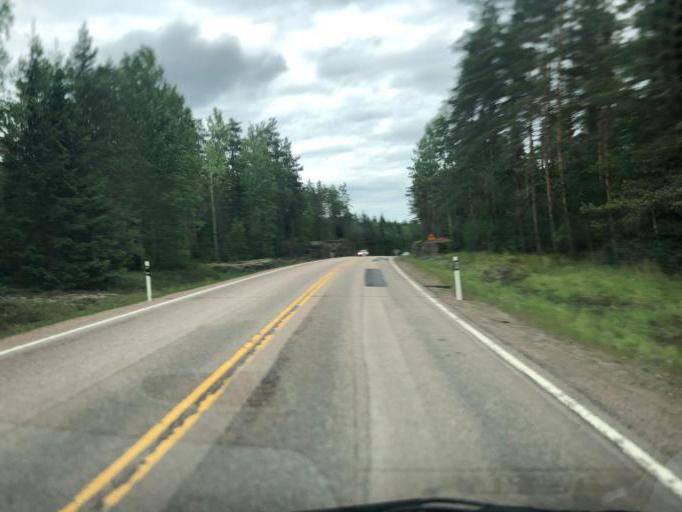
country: FI
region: Southern Savonia
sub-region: Mikkeli
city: Maentyharju
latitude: 61.1378
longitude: 27.1041
